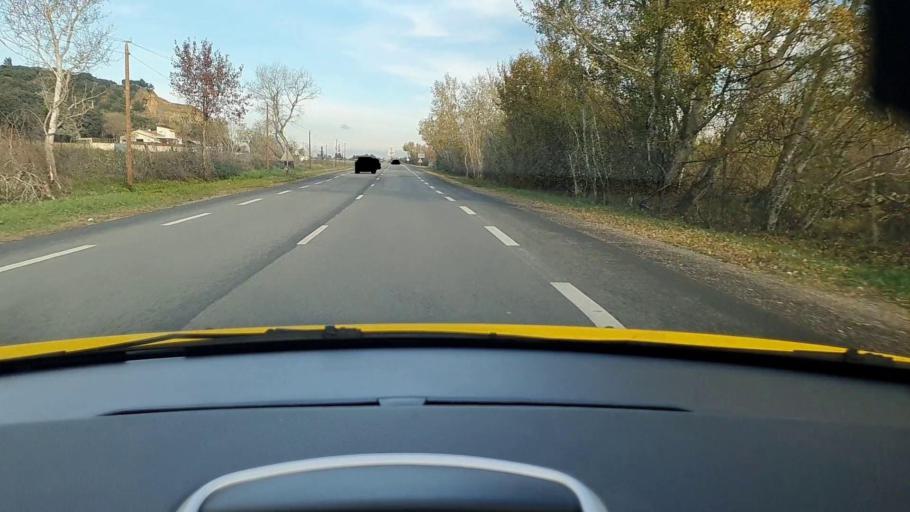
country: FR
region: Languedoc-Roussillon
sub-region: Departement du Gard
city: Vallabregues
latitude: 43.8375
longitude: 4.6211
